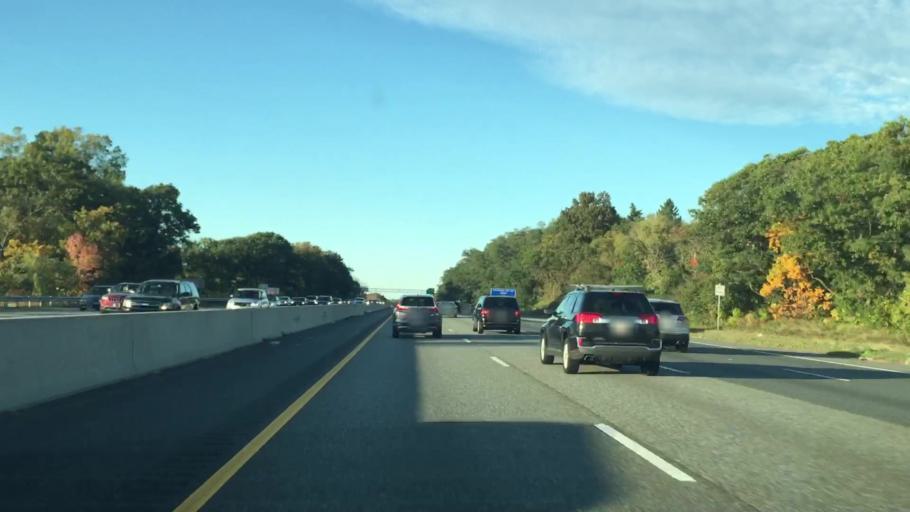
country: US
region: Massachusetts
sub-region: Middlesex County
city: Waltham
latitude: 42.4002
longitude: -71.2601
